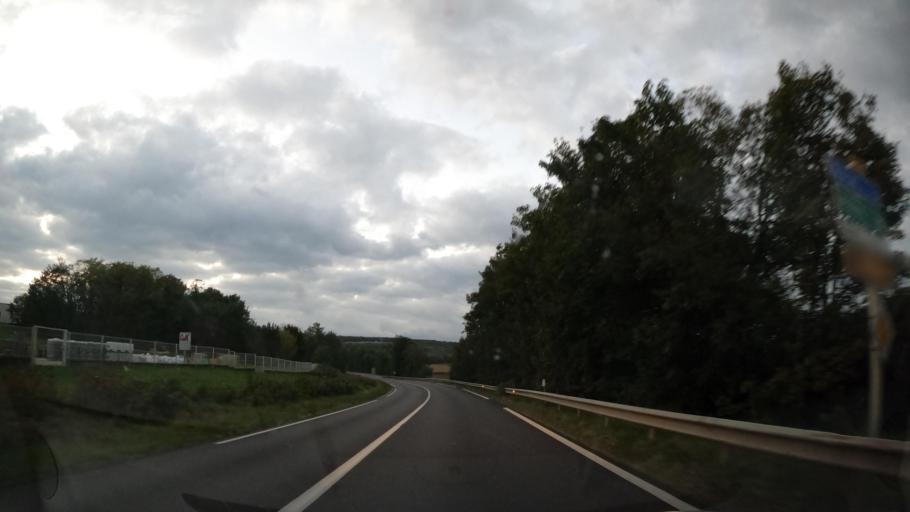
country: FR
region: Franche-Comte
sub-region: Departement du Jura
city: Dole
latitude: 47.1139
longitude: 5.5002
